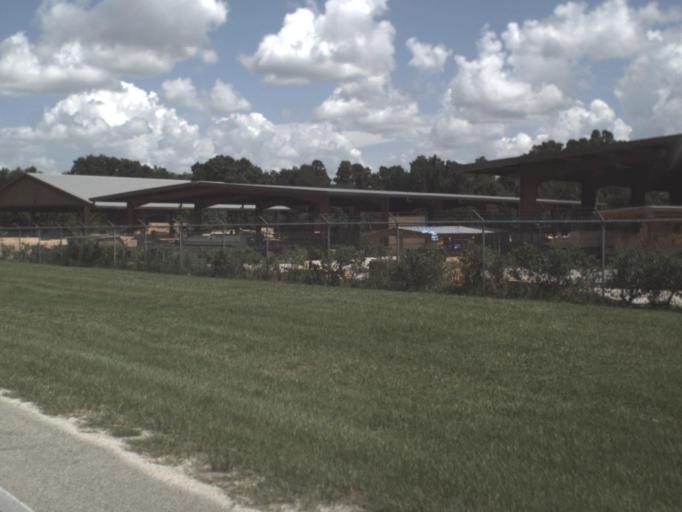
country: US
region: Florida
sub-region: Polk County
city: Bartow
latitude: 27.9119
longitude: -81.8274
